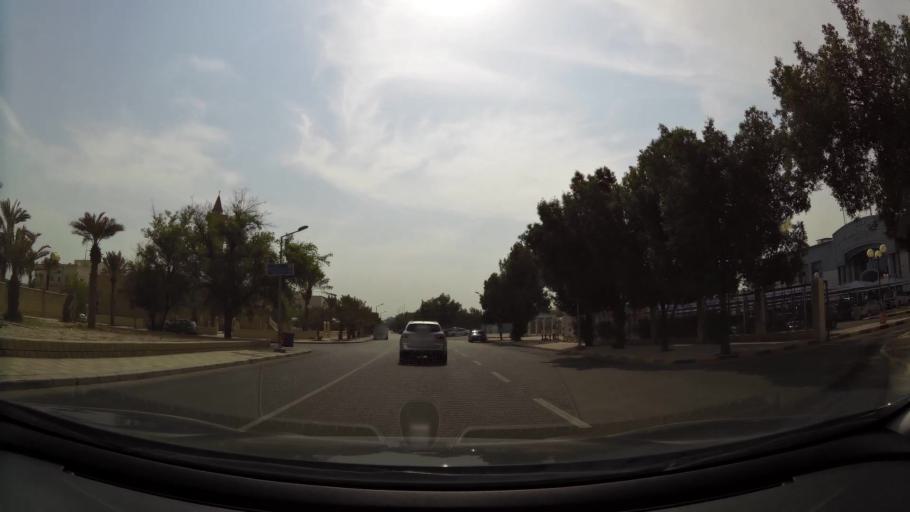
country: KW
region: Al Asimah
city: Ash Shamiyah
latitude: 29.3518
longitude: 47.9752
